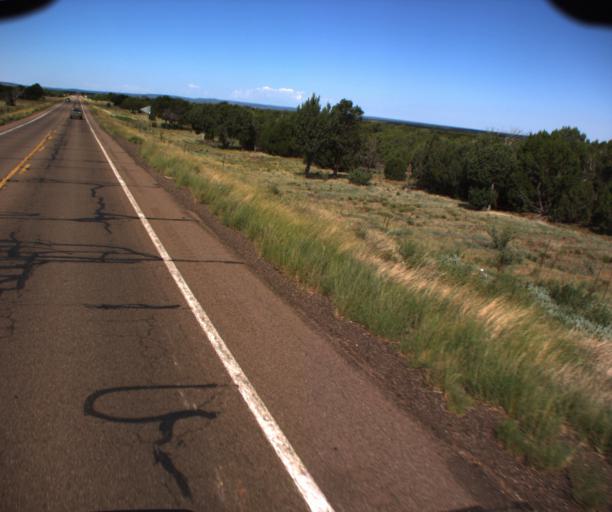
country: US
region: Arizona
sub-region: Navajo County
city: Show Low
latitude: 34.2707
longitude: -109.9244
